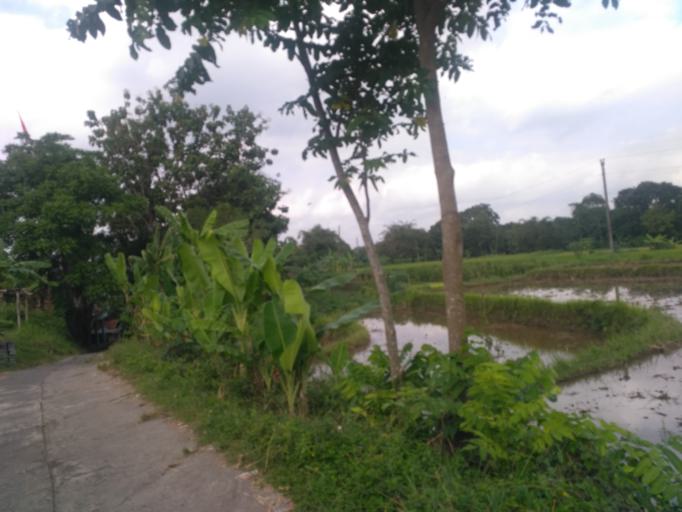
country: ID
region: Daerah Istimewa Yogyakarta
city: Yogyakarta
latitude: -7.7640
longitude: 110.3526
